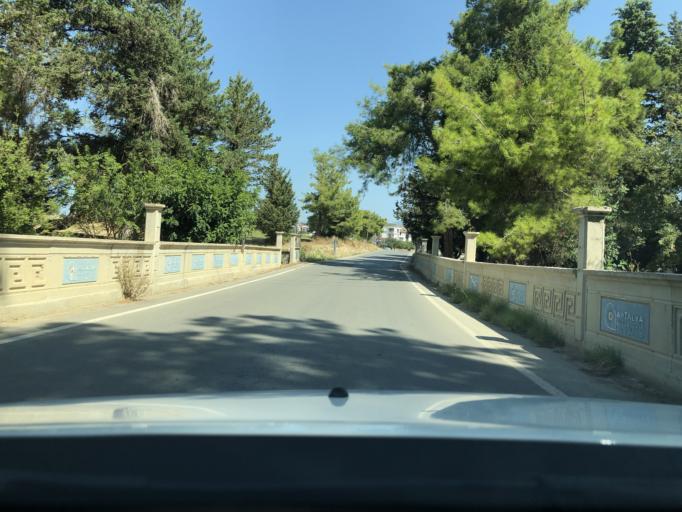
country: TR
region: Antalya
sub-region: Manavgat
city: Manavgat
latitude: 36.8162
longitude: 31.4889
